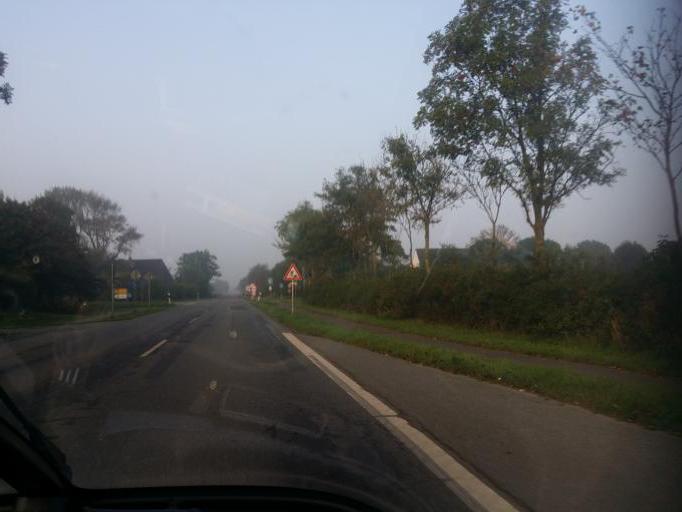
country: DE
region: Schleswig-Holstein
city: Elisabeth-Sophien-Koog
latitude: 54.4979
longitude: 8.9290
